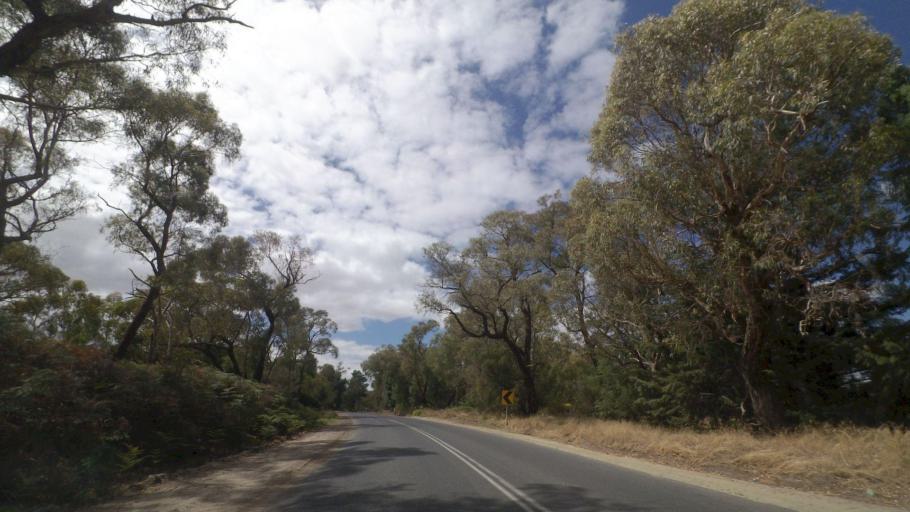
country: AU
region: Victoria
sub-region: Cardinia
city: Koo-Wee-Rup
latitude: -38.2916
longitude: 145.6245
